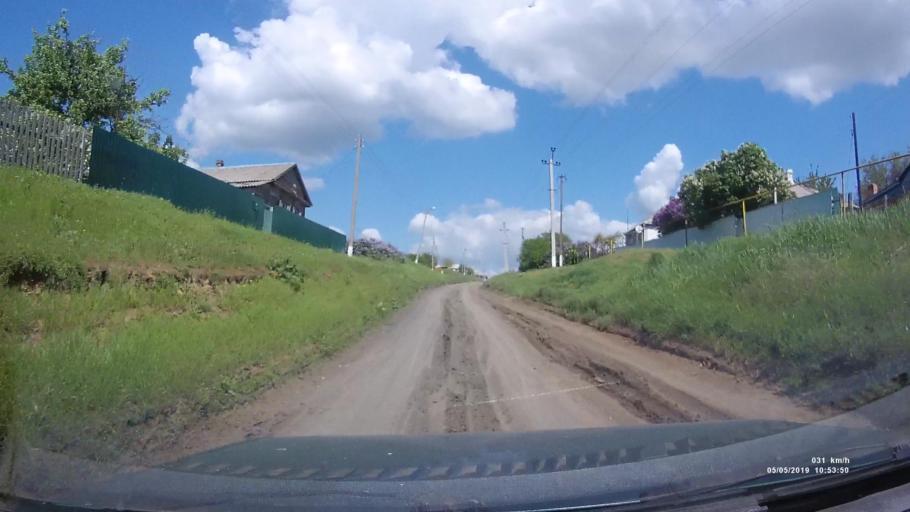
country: RU
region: Rostov
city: Ust'-Donetskiy
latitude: 47.6555
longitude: 40.8239
